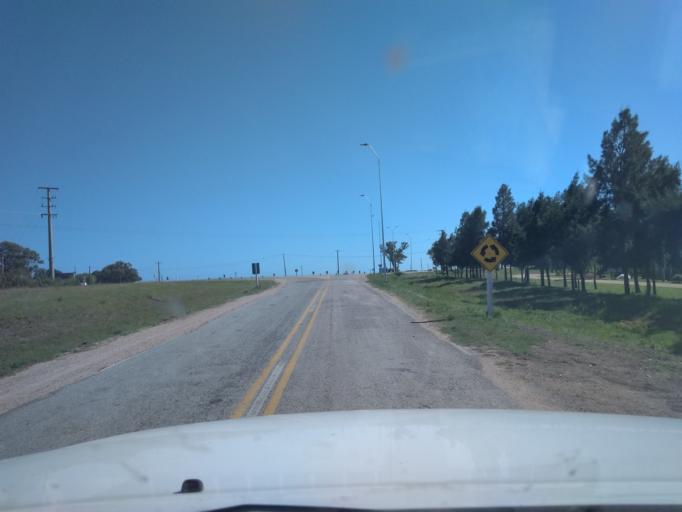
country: UY
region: Florida
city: Casupa
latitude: -34.0380
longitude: -55.8878
